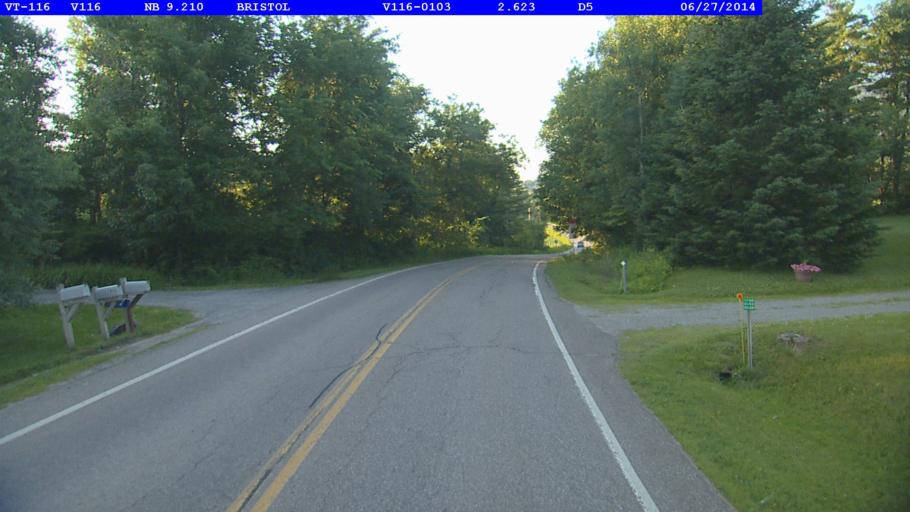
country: US
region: Vermont
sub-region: Addison County
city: Bristol
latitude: 44.0909
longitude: -73.0916
